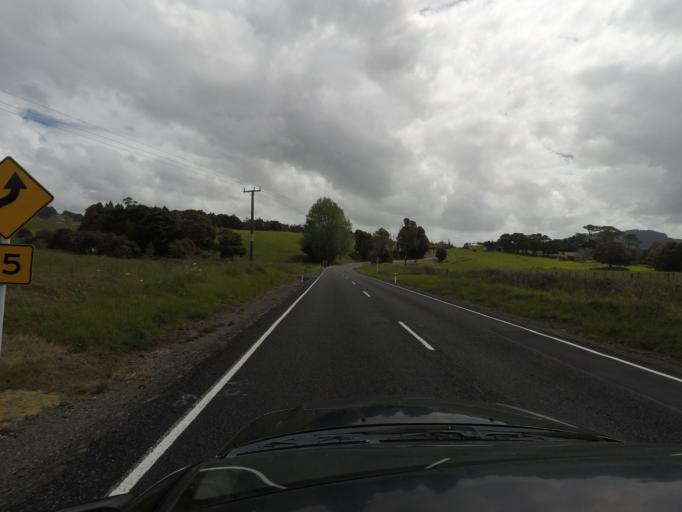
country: NZ
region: Auckland
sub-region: Auckland
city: Parakai
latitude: -36.5021
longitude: 174.5132
